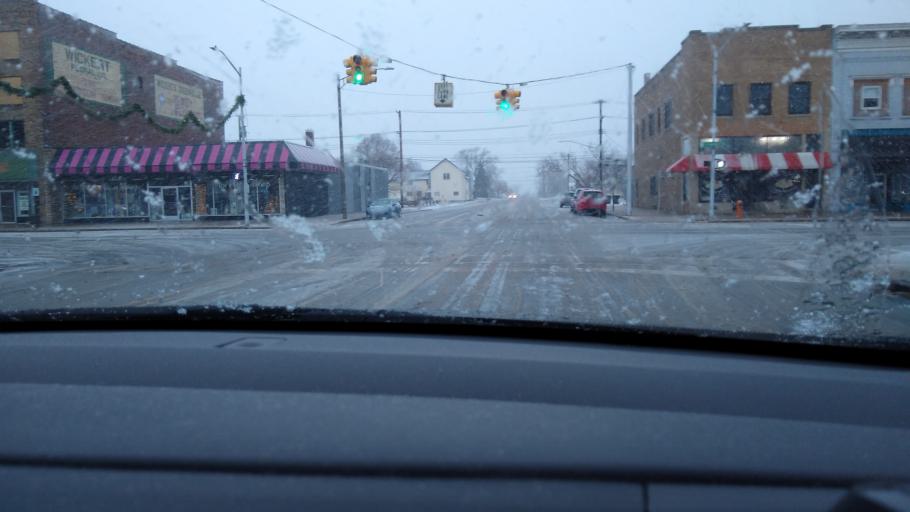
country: US
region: Michigan
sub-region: Delta County
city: Escanaba
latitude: 45.7455
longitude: -87.0612
